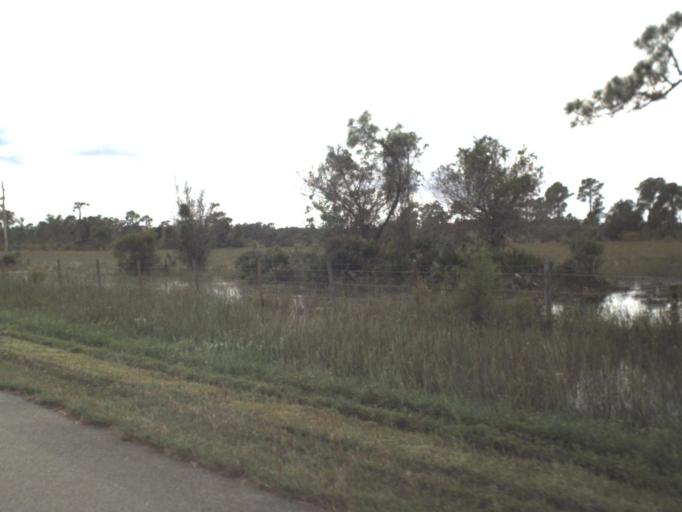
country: US
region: Florida
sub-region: Lee County
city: Olga
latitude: 26.9184
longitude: -81.7605
